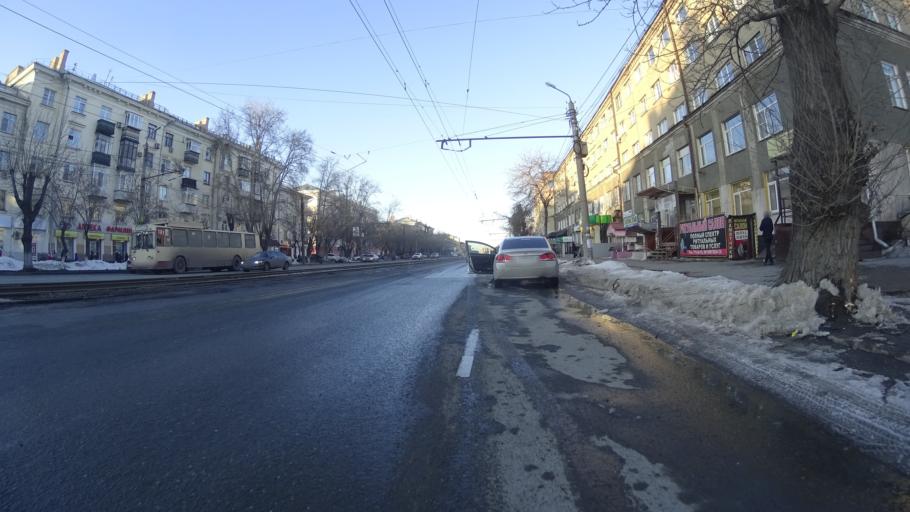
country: RU
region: Chelyabinsk
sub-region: Gorod Chelyabinsk
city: Chelyabinsk
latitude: 55.1416
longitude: 61.4426
